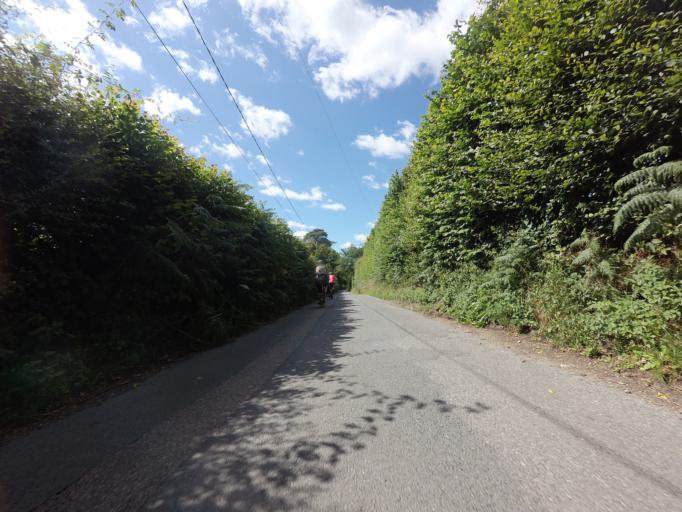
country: GB
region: England
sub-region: East Sussex
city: Horam
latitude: 50.9134
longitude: 0.2166
